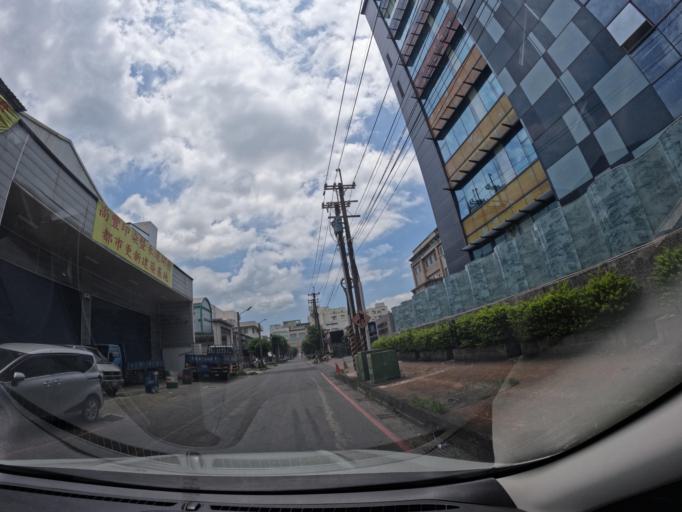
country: TW
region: Taipei
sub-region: Taipei
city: Banqiao
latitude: 24.9667
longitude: 121.4258
